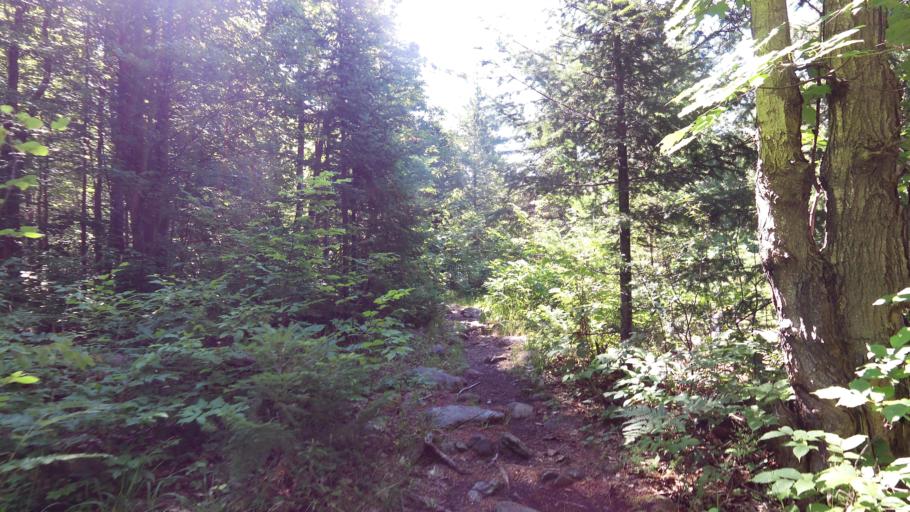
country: CA
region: Ontario
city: Arnprior
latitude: 45.4626
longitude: -76.2654
